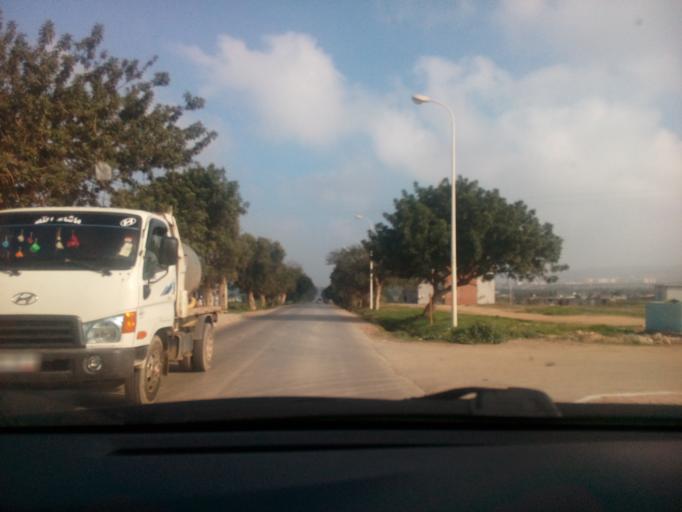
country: DZ
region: Oran
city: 'Ain el Turk
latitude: 35.7057
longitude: -0.8068
